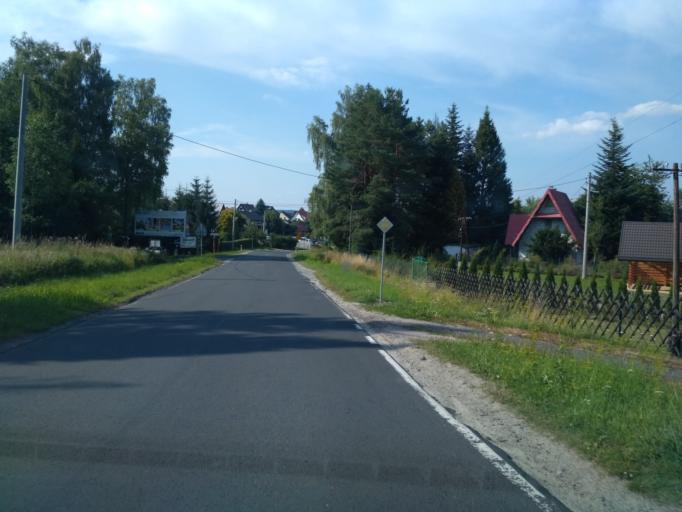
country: PL
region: Subcarpathian Voivodeship
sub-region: Powiat bieszczadzki
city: Czarna
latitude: 49.3102
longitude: 22.6732
